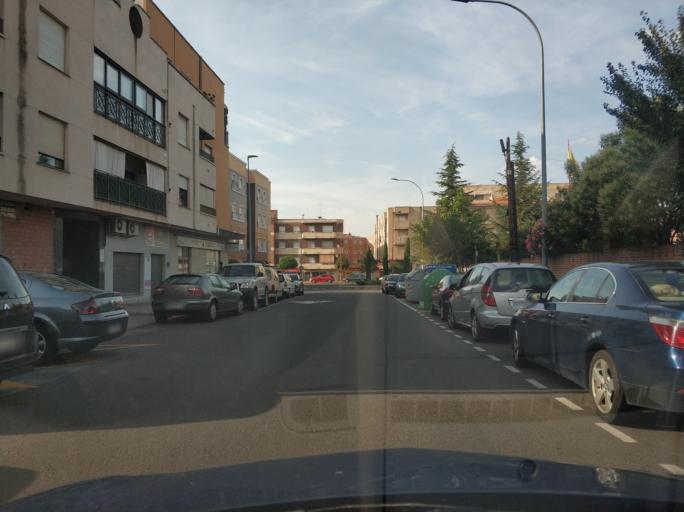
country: ES
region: Castille and Leon
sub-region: Provincia de Salamanca
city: Santa Marta de Tormes
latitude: 40.9493
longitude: -5.6264
